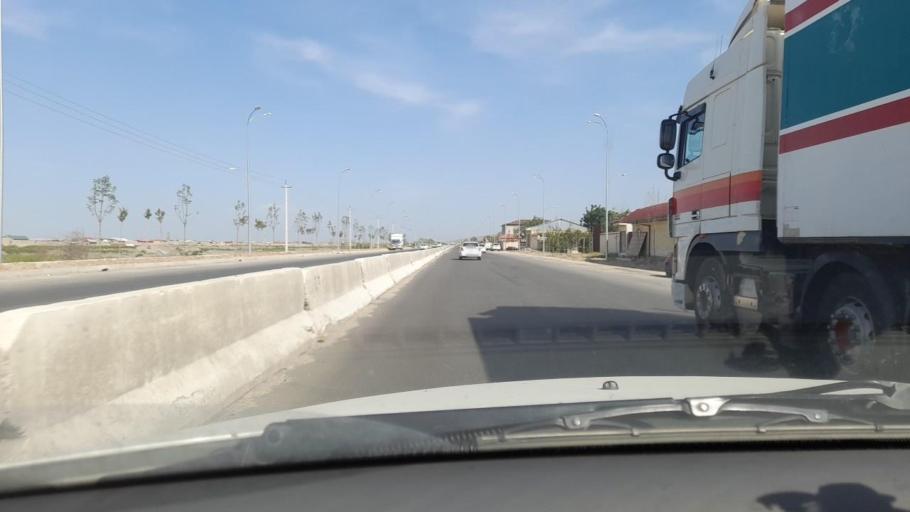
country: UZ
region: Samarqand
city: Samarqand
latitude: 39.7101
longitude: 66.9806
